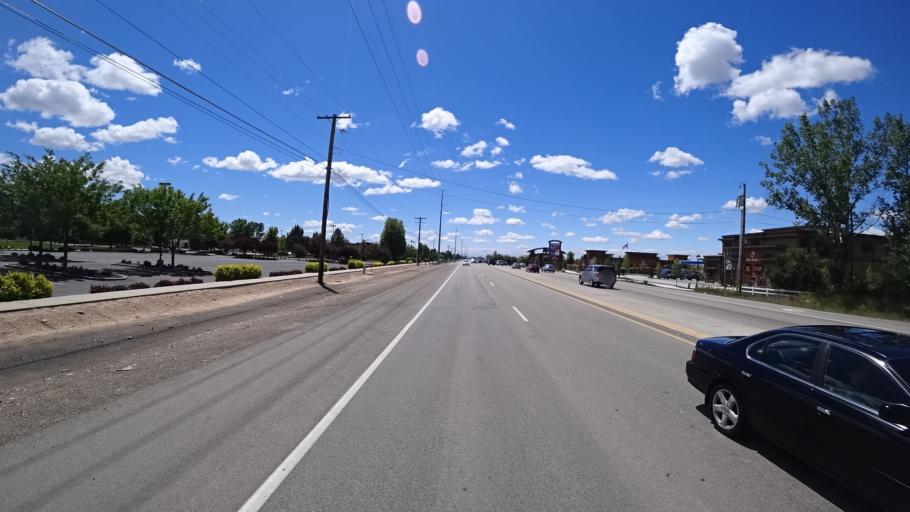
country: US
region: Idaho
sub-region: Ada County
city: Meridian
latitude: 43.6395
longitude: -116.3542
